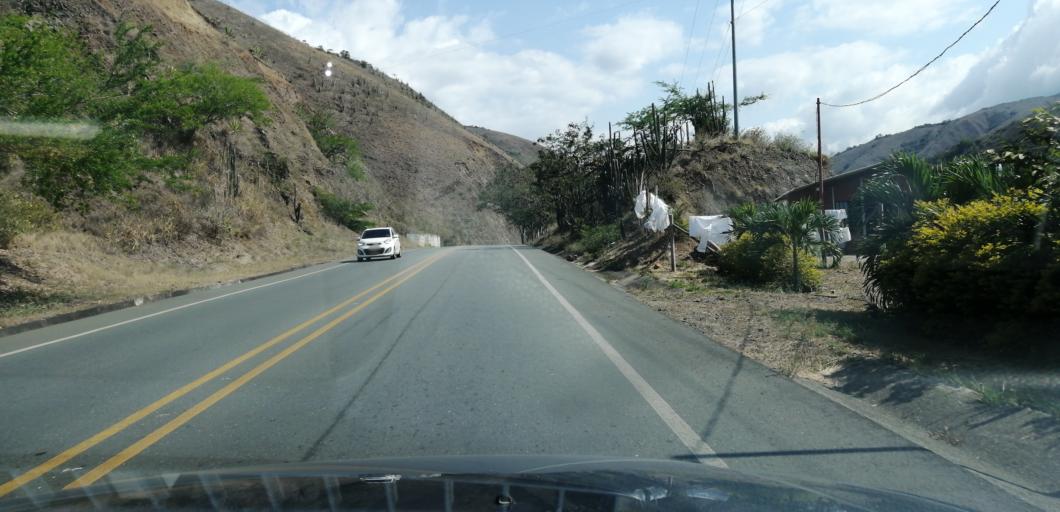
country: CO
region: Valle del Cauca
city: Dagua
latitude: 3.7382
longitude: -76.6648
